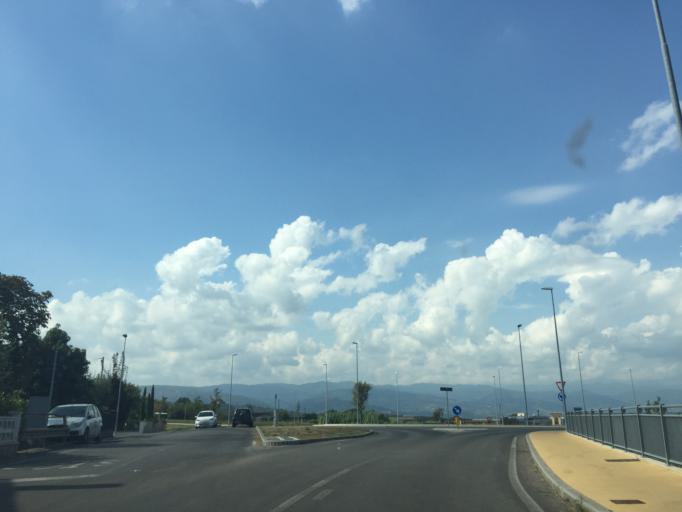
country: IT
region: Tuscany
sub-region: Provincia di Pistoia
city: Cantagrillo-Casalguidi
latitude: 43.8788
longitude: 10.9101
